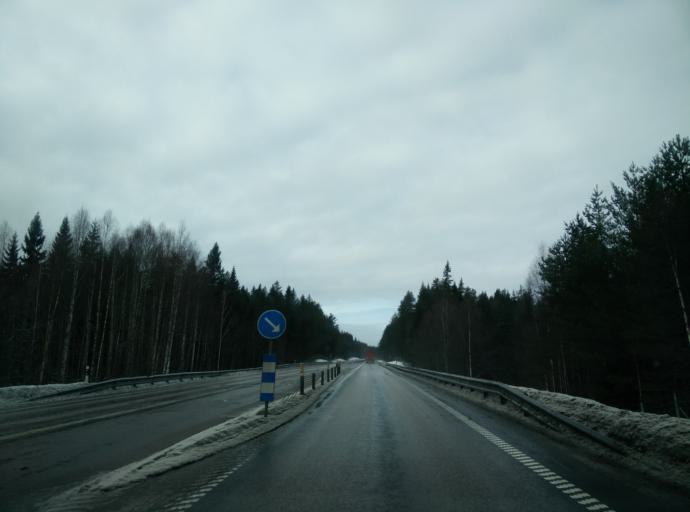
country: SE
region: Dalarna
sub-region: Hedemora Kommun
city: Langshyttan
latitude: 60.5548
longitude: 16.0967
